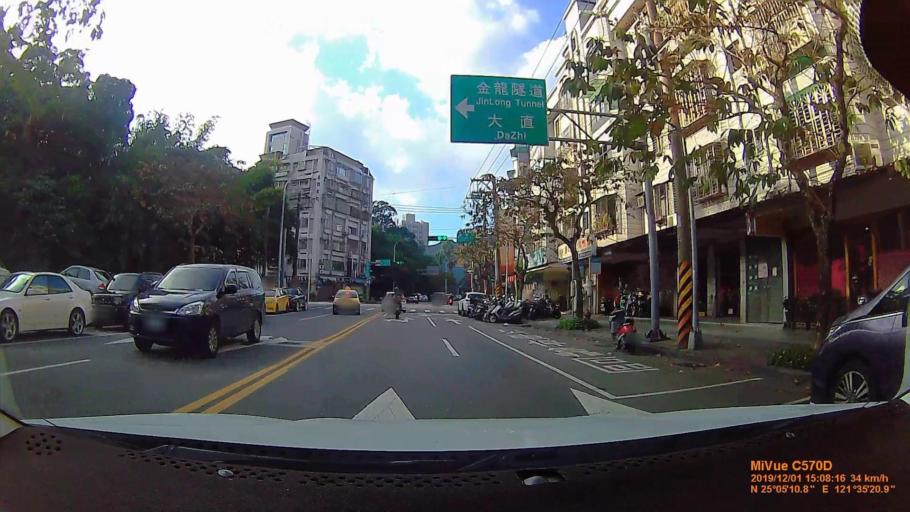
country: TW
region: Taipei
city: Taipei
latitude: 25.0863
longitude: 121.5891
